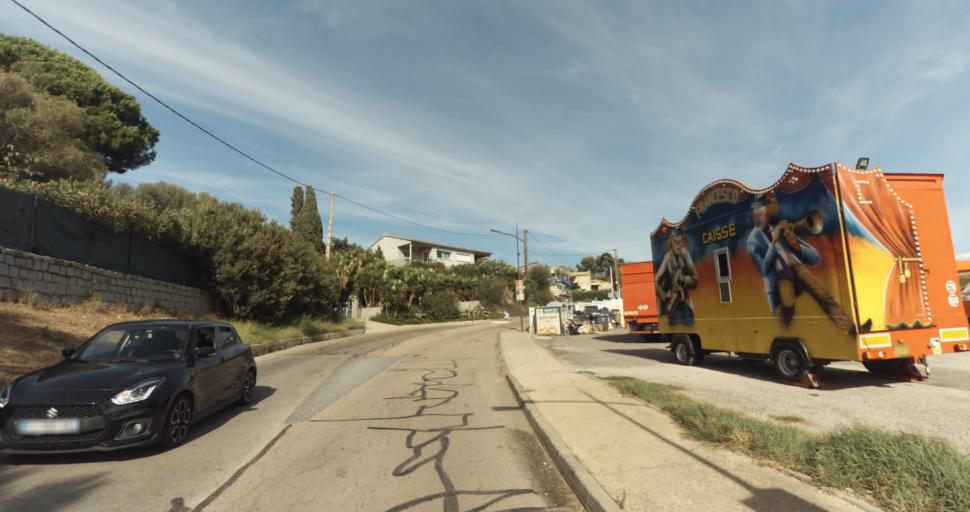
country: FR
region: Corsica
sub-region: Departement de la Corse-du-Sud
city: Afa
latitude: 41.9236
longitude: 8.8227
